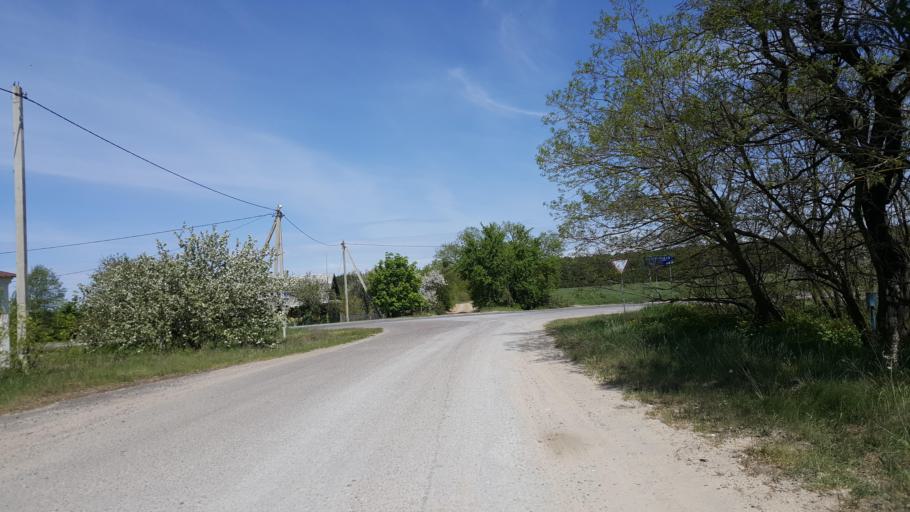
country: BY
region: Brest
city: Zhabinka
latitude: 52.3594
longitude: 24.1565
